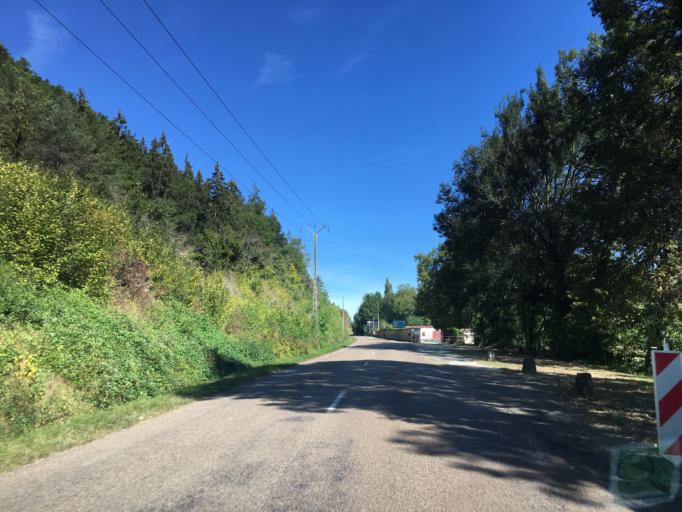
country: FR
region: Bourgogne
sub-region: Departement de l'Yonne
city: Vermenton
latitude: 47.6399
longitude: 3.6578
